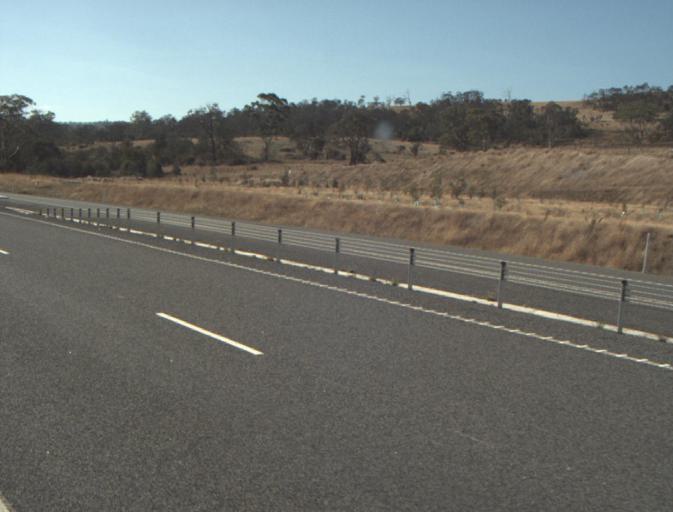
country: AU
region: Tasmania
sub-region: Launceston
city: Mayfield
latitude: -41.3544
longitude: 147.1039
